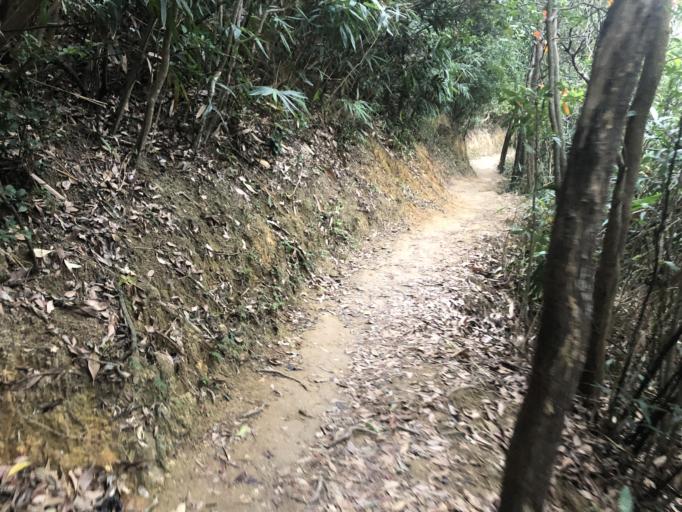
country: HK
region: Wanchai
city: Wan Chai
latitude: 22.2775
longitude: 114.2110
